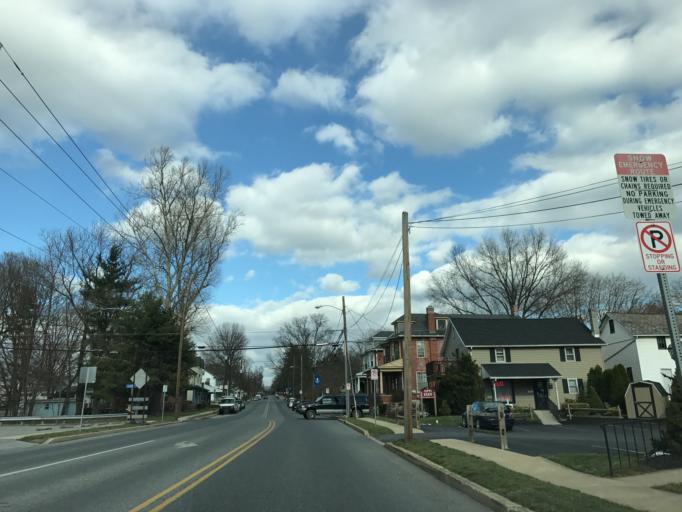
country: US
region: Pennsylvania
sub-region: Lancaster County
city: Elizabethtown
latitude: 40.1470
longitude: -76.6028
